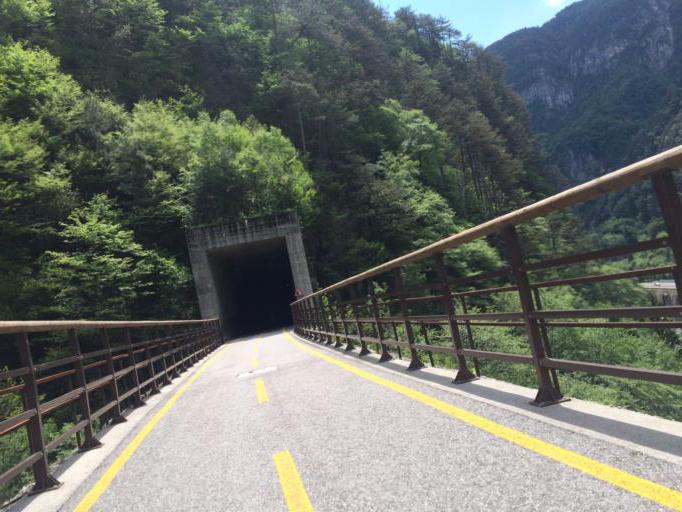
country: IT
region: Friuli Venezia Giulia
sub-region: Provincia di Udine
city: Dogna
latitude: 46.4654
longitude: 13.2949
